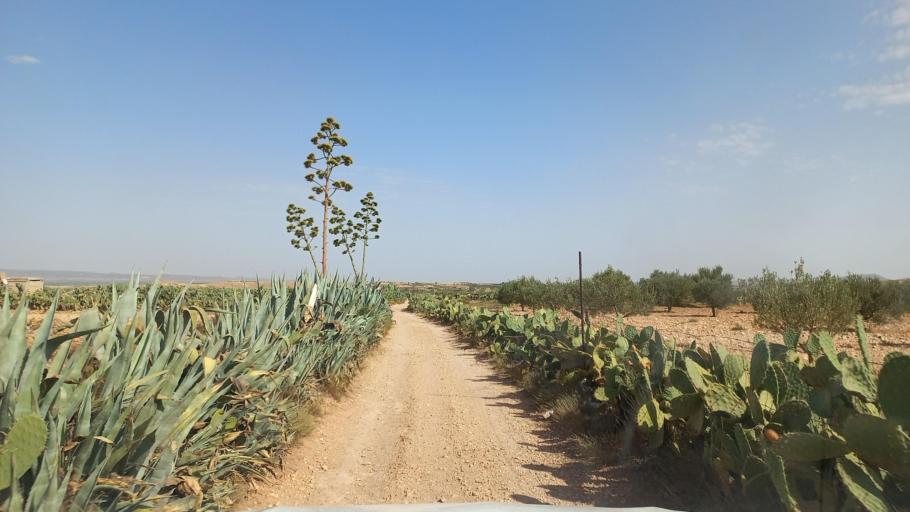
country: TN
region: Al Qasrayn
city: Kasserine
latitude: 35.2830
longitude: 8.9475
